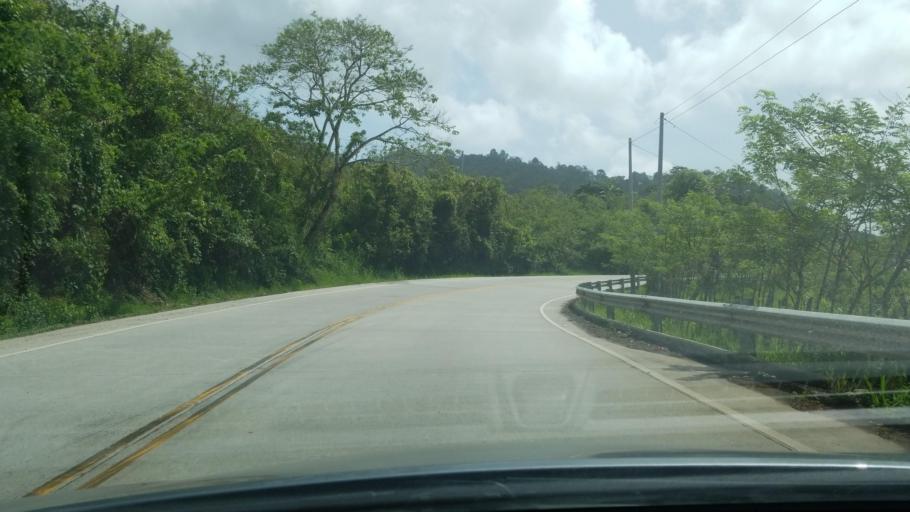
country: HN
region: Copan
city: San Jeronimo
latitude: 14.9290
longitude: -88.9371
